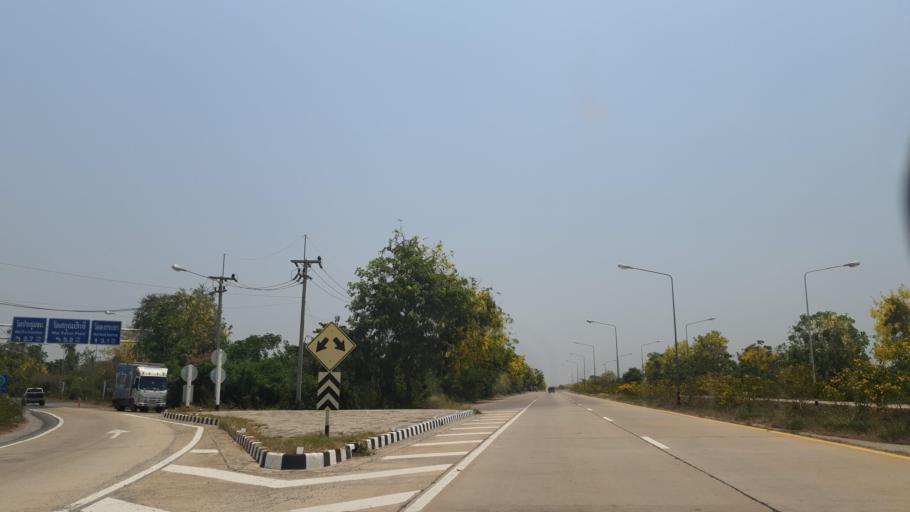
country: TH
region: Suphan Buri
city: Suphan Buri
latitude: 14.5414
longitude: 100.0704
